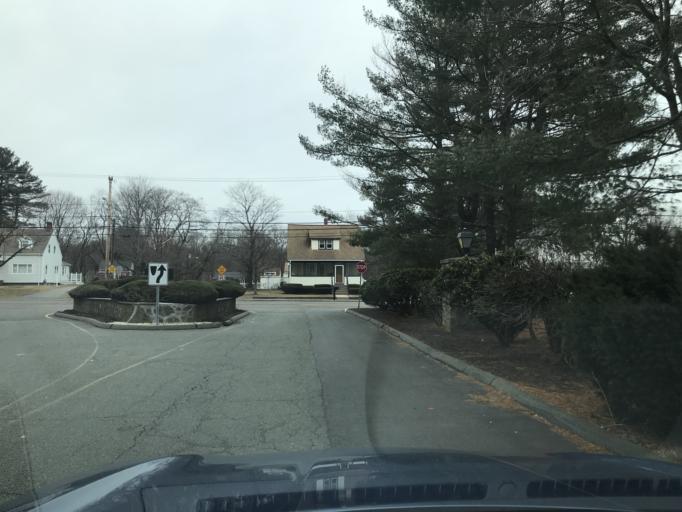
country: US
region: Massachusetts
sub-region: Essex County
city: Saugus
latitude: 42.4972
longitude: -71.0199
